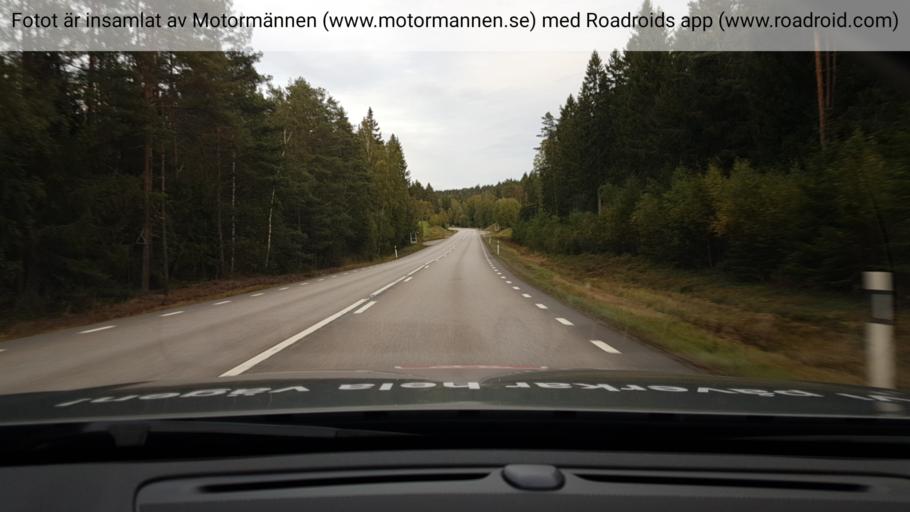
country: SE
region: Vaestra Goetaland
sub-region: Bengtsfors Kommun
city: Dals Langed
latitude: 59.0277
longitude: 12.3960
